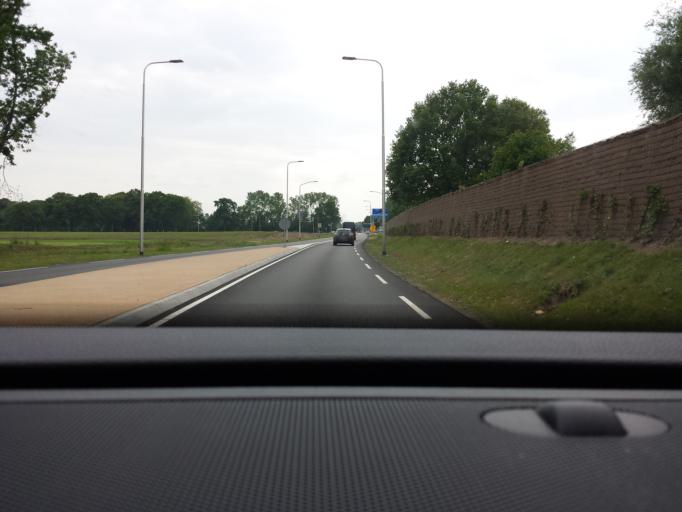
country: NL
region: Gelderland
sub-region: Gemeente Doetinchem
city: Doetinchem
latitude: 51.9710
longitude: 6.3215
